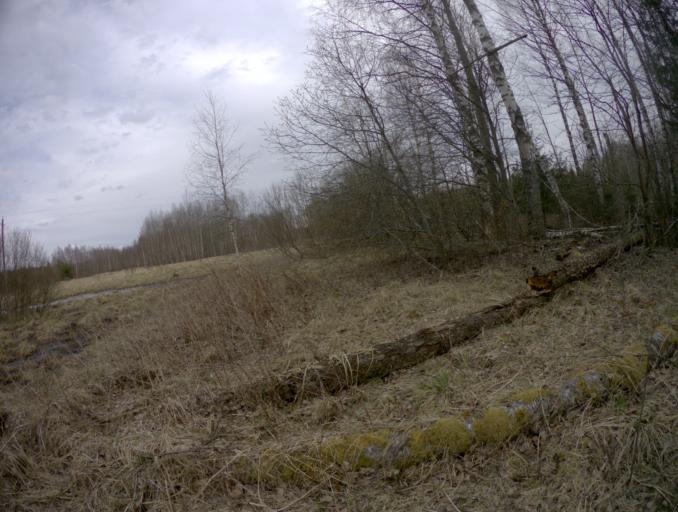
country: RU
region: Vladimir
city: Raduzhnyy
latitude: 55.8771
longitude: 40.2090
